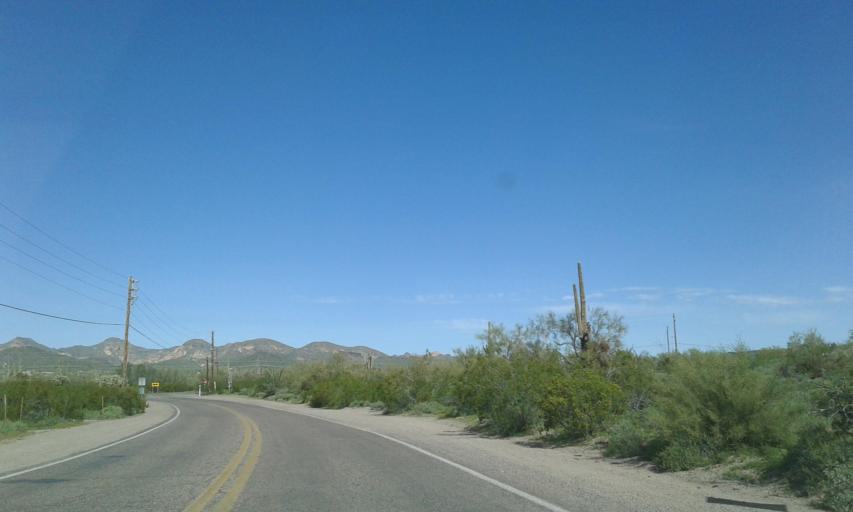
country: US
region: Arizona
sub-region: Pinal County
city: Apache Junction
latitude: 33.4514
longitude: -111.4943
